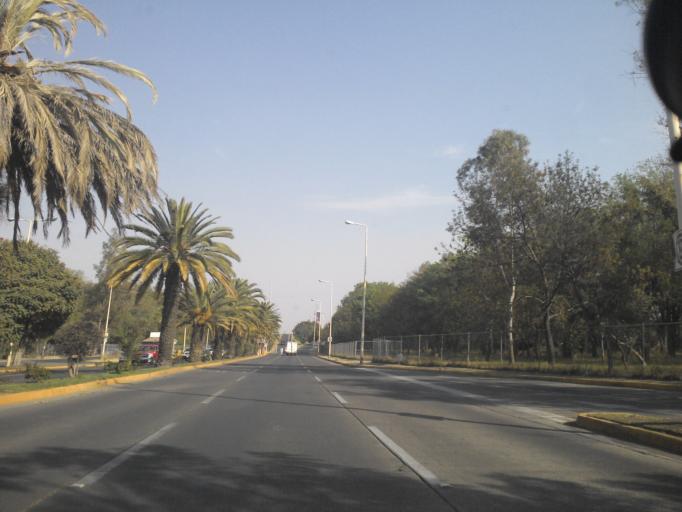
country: MX
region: Jalisco
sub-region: Tlajomulco de Zuniga
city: La Tijera
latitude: 20.6037
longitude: -103.4383
